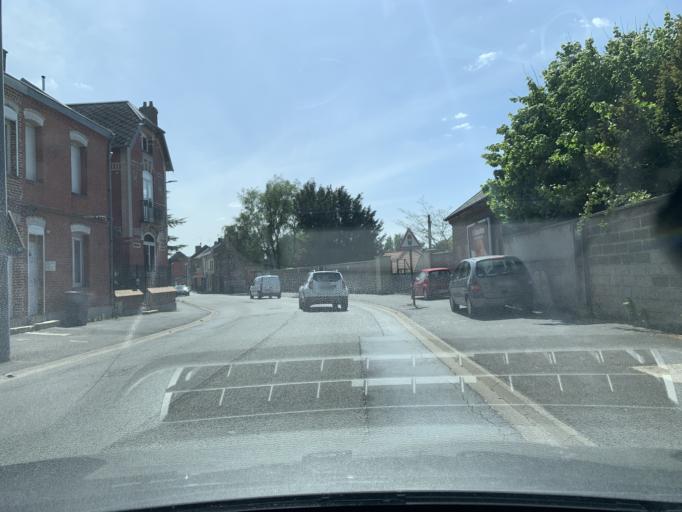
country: FR
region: Picardie
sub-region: Departement de l'Aisne
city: Saint-Quentin
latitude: 49.8608
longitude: 3.2903
